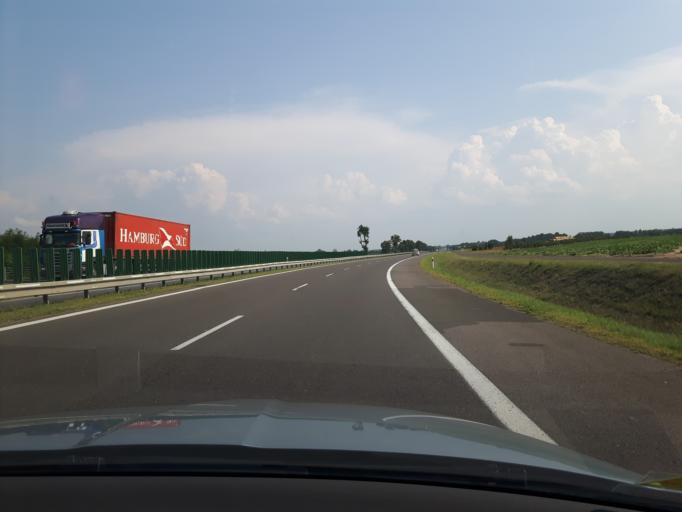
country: PL
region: Masovian Voivodeship
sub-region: Powiat plonski
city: Zaluski
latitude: 52.5774
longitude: 20.4801
